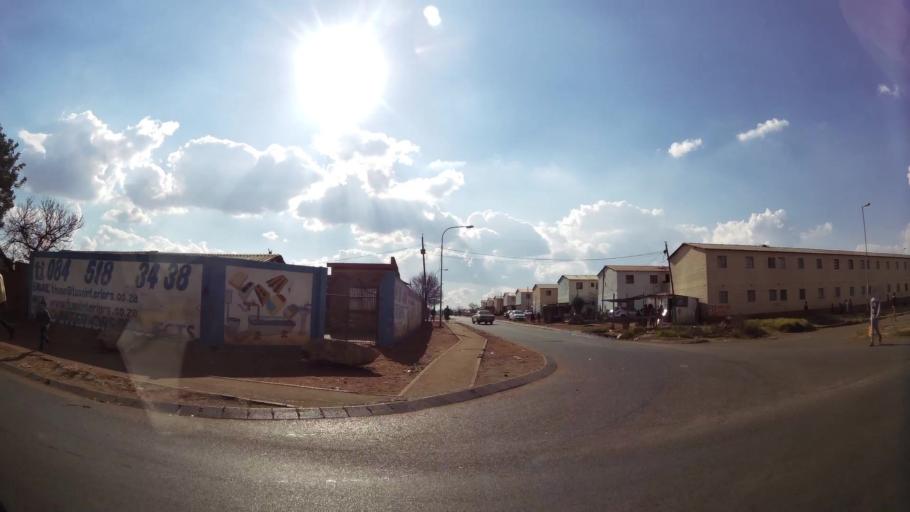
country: ZA
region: Gauteng
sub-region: City of Johannesburg Metropolitan Municipality
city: Soweto
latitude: -26.2187
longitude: 27.8644
